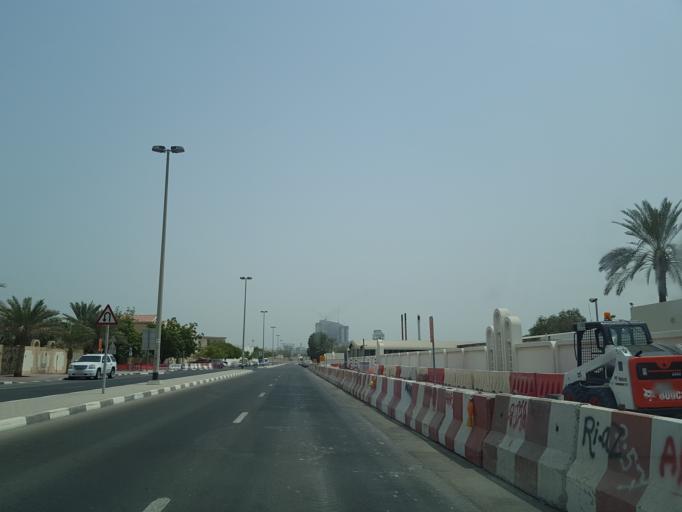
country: AE
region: Ash Shariqah
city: Sharjah
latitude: 25.2371
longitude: 55.2914
